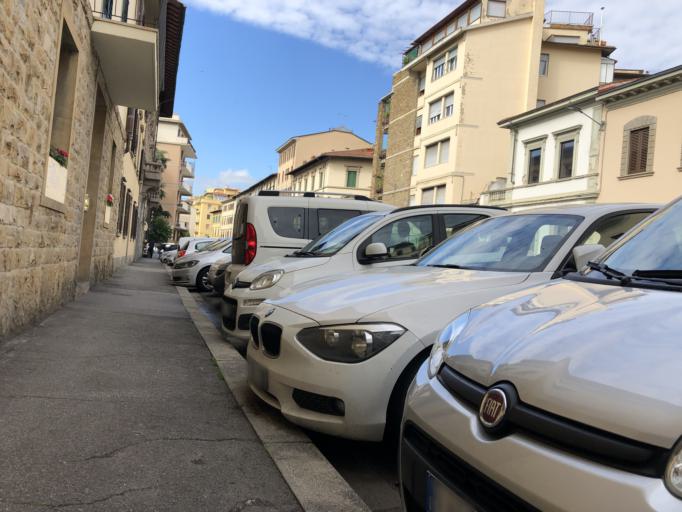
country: IT
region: Tuscany
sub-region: Province of Florence
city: Florence
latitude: 43.7742
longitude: 11.2743
